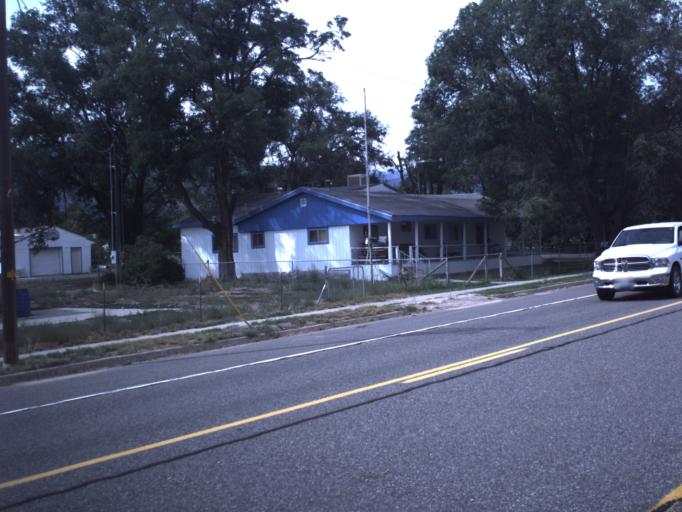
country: US
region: Utah
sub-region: Piute County
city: Junction
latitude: 38.2406
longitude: -112.2200
